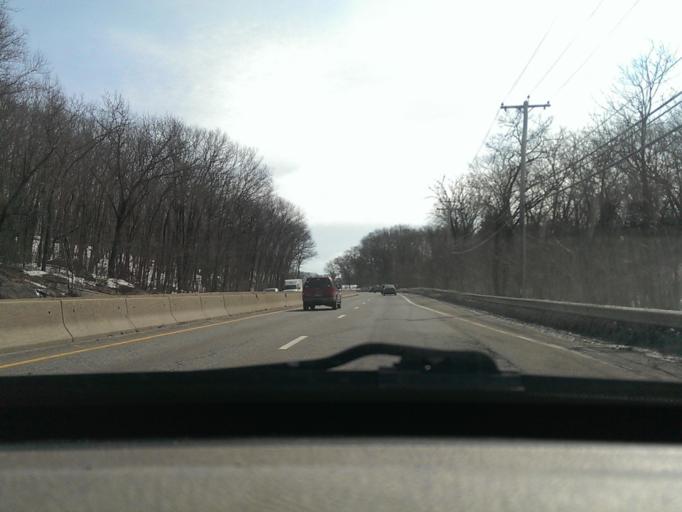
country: US
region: Massachusetts
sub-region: Worcester County
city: Millbury
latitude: 42.1838
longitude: -71.7629
